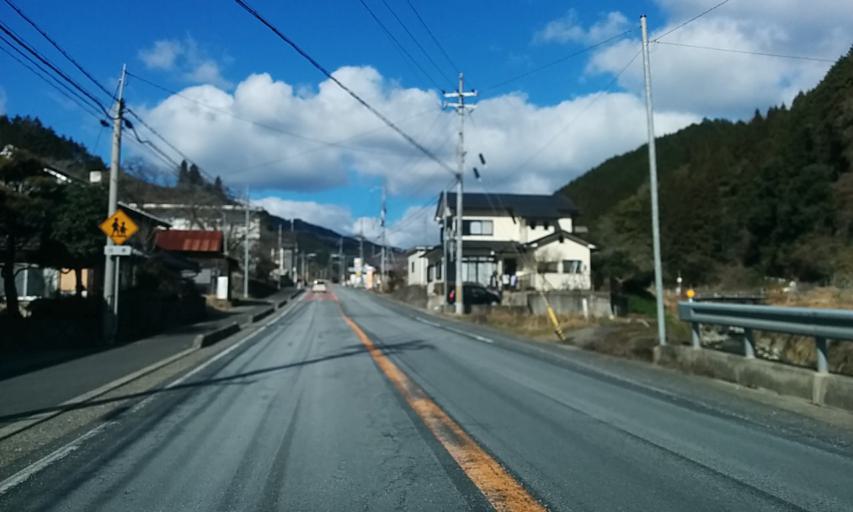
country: JP
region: Kyoto
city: Fukuchiyama
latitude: 35.3655
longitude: 135.0504
